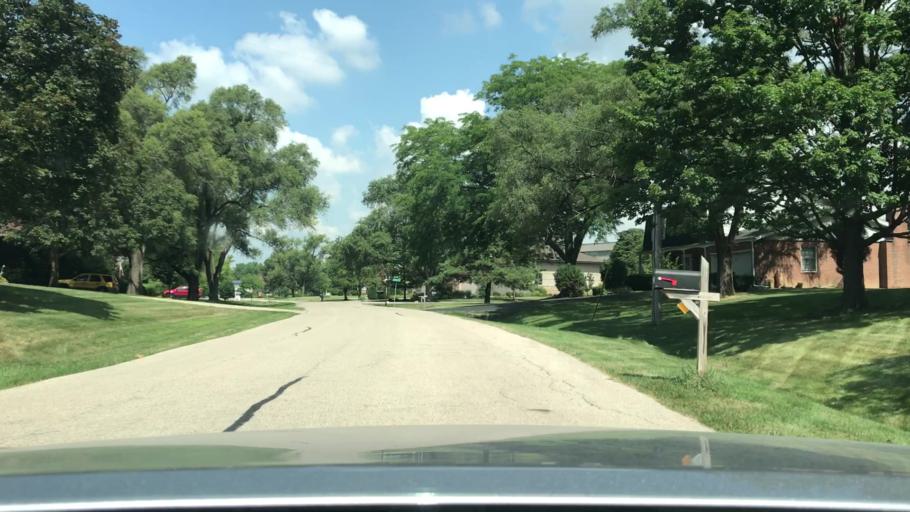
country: US
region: Illinois
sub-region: DuPage County
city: Darien
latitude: 41.7307
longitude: -88.0026
